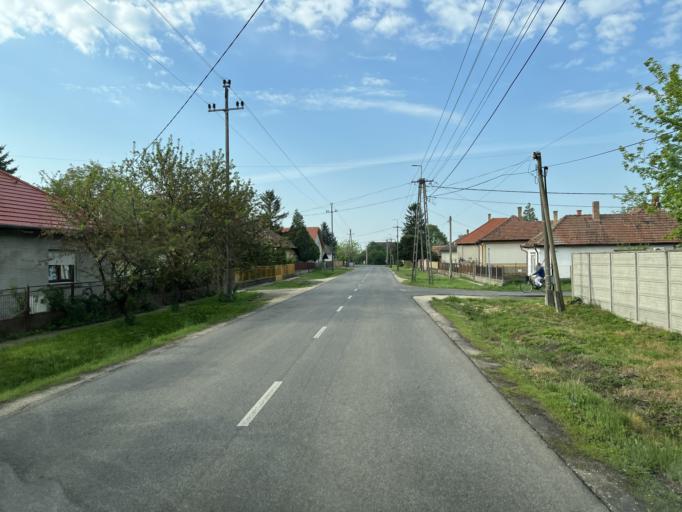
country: HU
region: Pest
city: Abony
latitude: 47.1994
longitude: 20.0133
